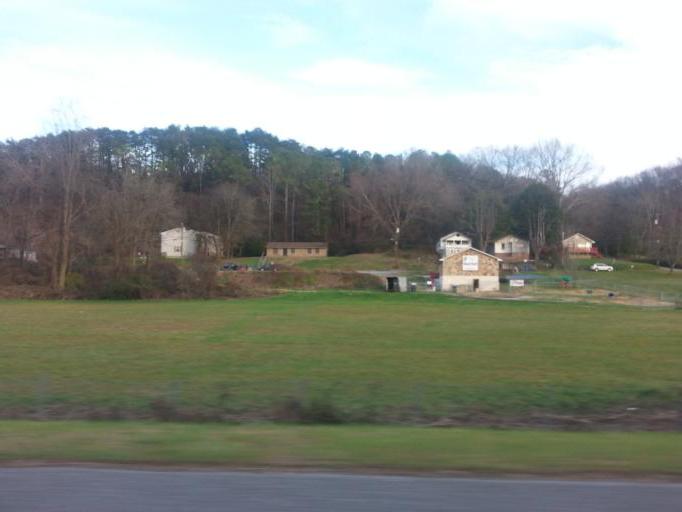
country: US
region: Tennessee
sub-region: Rhea County
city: Dayton
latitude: 35.5003
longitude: -85.0059
